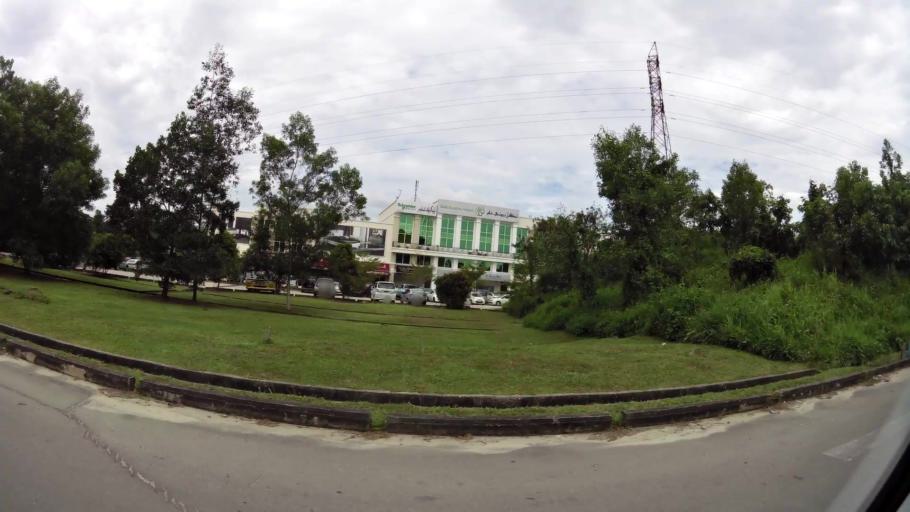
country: BN
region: Brunei and Muara
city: Bandar Seri Begawan
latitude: 4.8868
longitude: 114.8974
